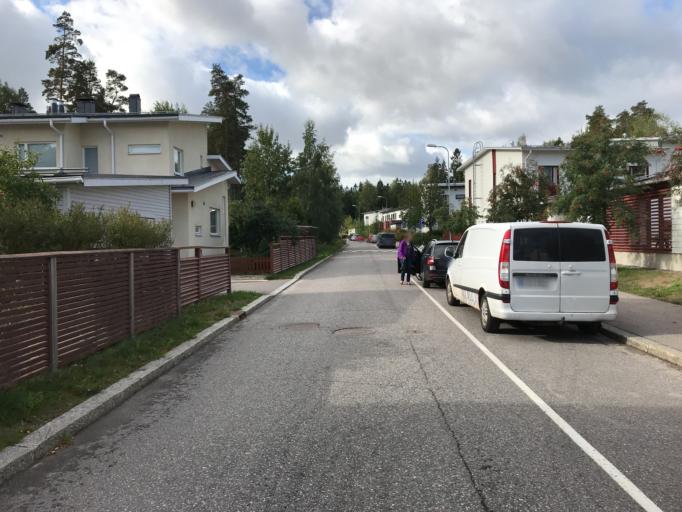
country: FI
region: Uusimaa
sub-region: Helsinki
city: Vantaa
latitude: 60.2250
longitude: 25.0508
